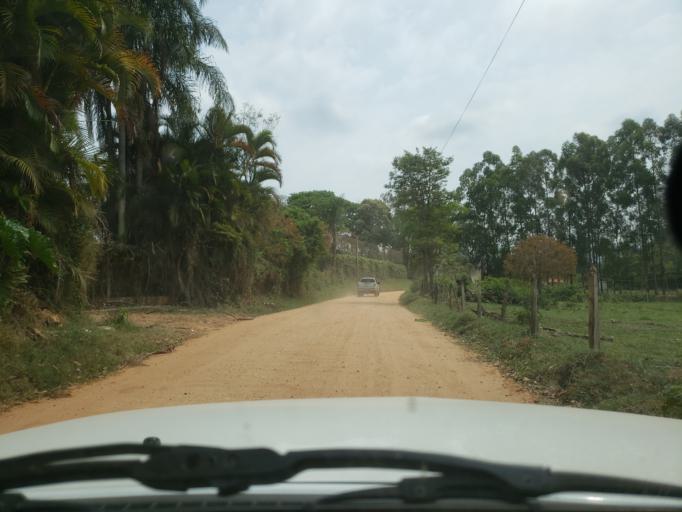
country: BR
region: Minas Gerais
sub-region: Jacutinga
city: Jacutinga
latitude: -22.3084
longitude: -46.6066
